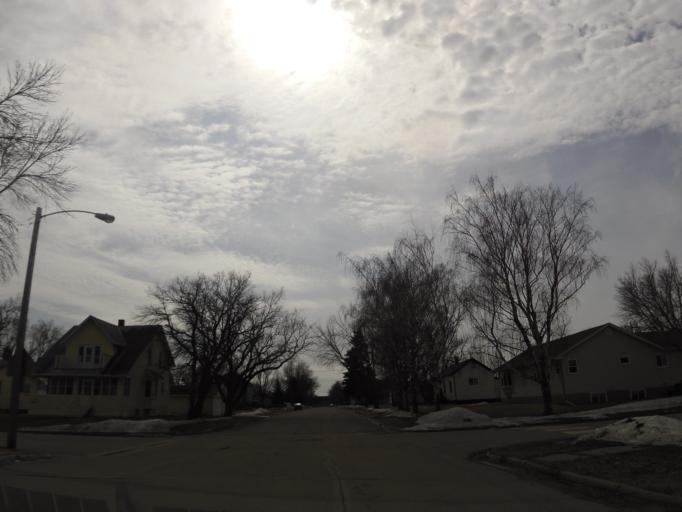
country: US
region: North Dakota
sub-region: Walsh County
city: Grafton
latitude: 48.2928
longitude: -97.3746
